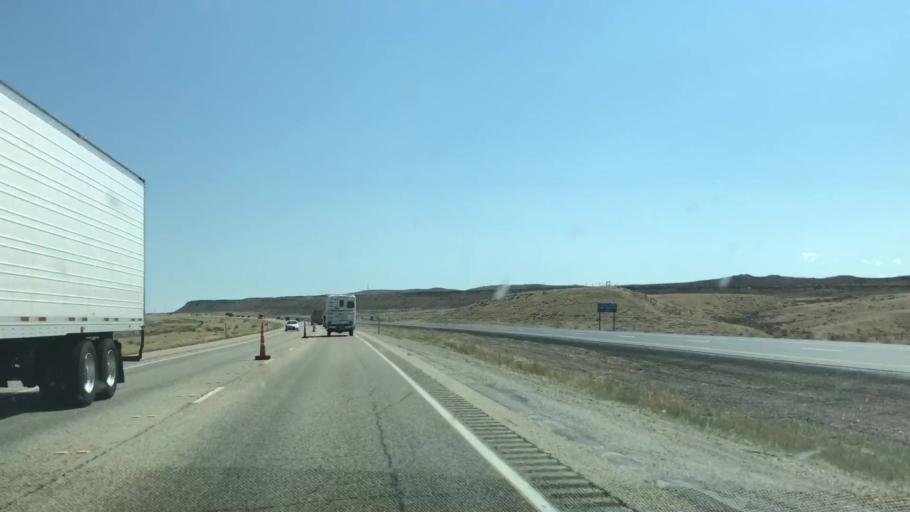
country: US
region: Wyoming
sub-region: Carbon County
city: Rawlins
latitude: 41.7461
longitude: -106.9316
